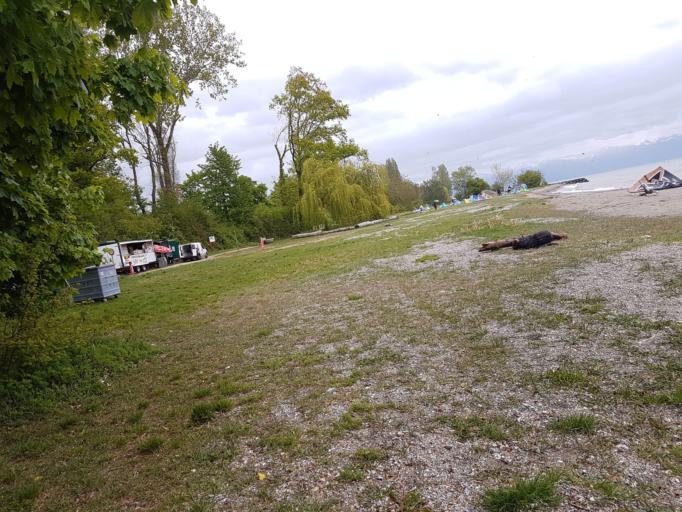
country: CH
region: Vaud
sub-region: Morges District
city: Preverenges
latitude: 46.5080
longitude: 6.5439
